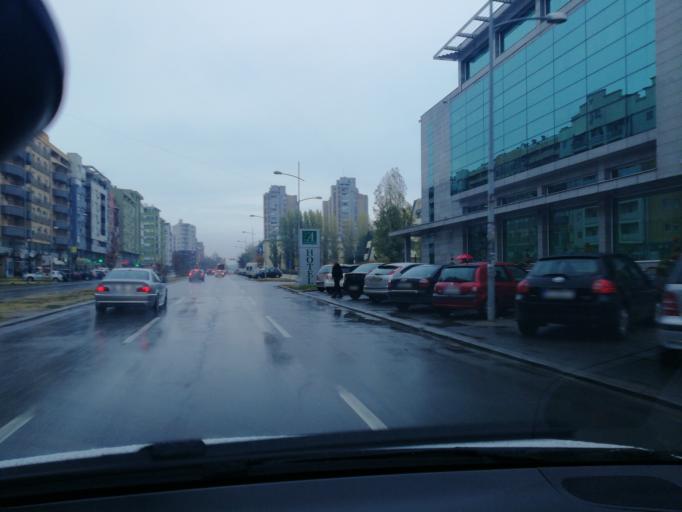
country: RS
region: Autonomna Pokrajina Vojvodina
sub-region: Juznobacki Okrug
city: Novi Sad
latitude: 45.2407
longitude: 19.8284
